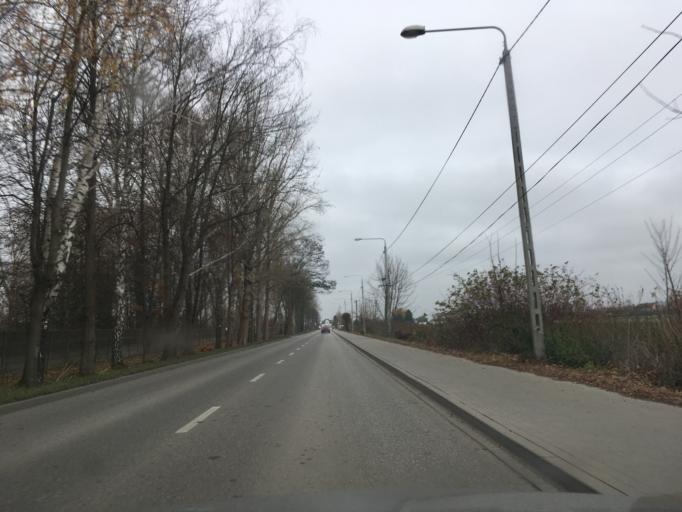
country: PL
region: Masovian Voivodeship
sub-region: Powiat piaseczynski
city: Lesznowola
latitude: 52.0827
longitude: 20.9395
